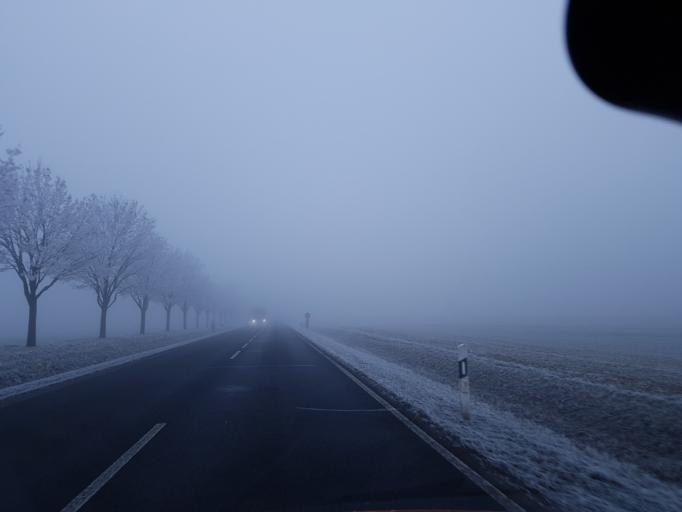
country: DE
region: Brandenburg
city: Muhlberg
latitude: 51.4589
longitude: 13.2393
